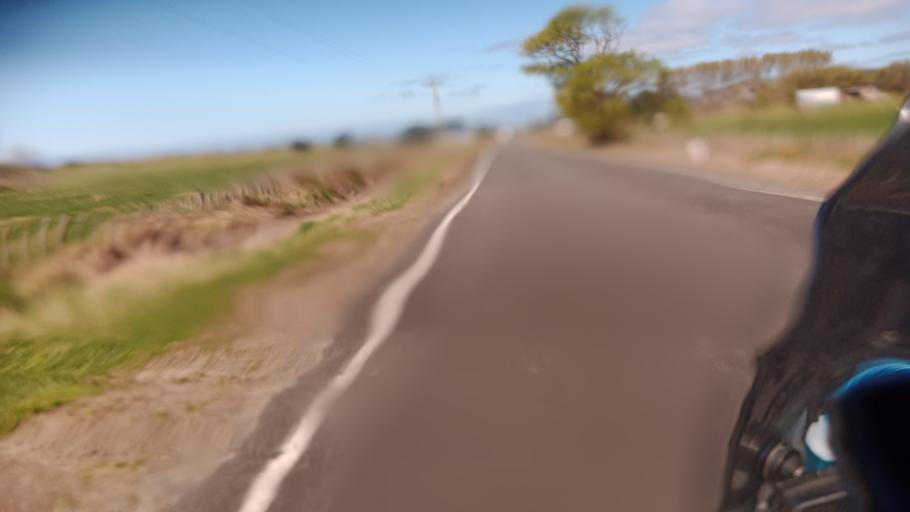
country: NZ
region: Gisborne
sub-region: Gisborne District
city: Gisborne
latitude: -39.0456
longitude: 177.8621
